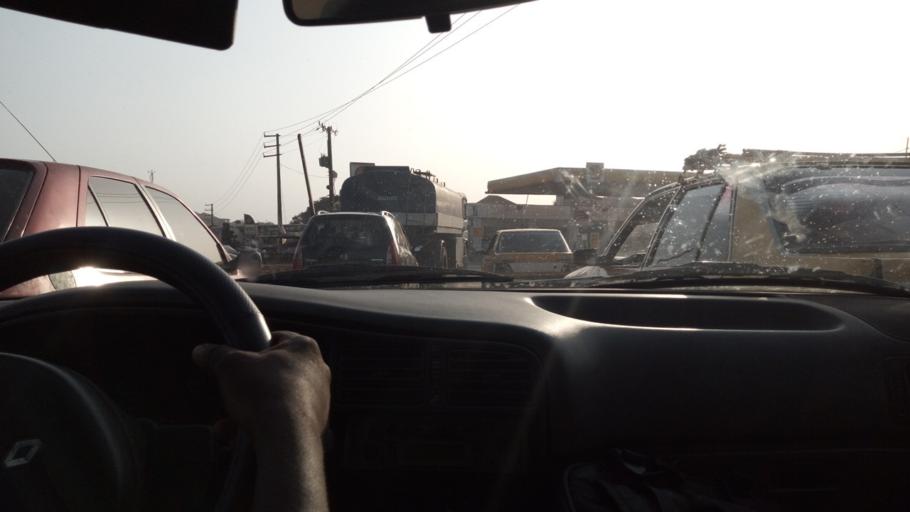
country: GN
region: Kindia
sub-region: Prefecture de Dubreka
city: Dubreka
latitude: 9.6769
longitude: -13.5437
